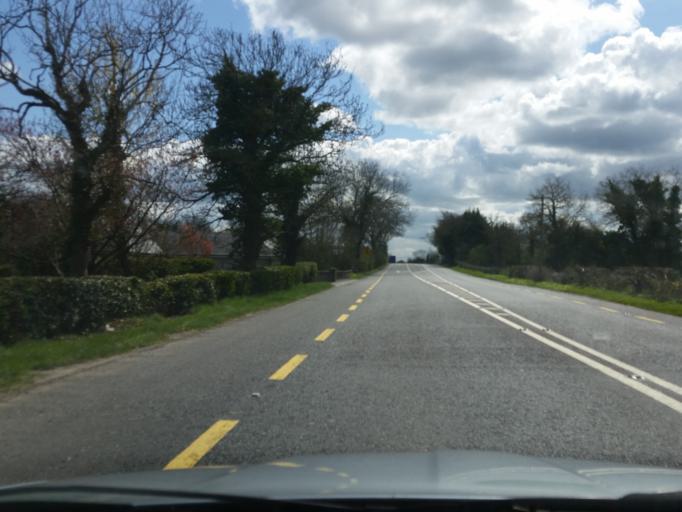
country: IE
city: Kentstown
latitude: 53.6683
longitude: -6.5315
